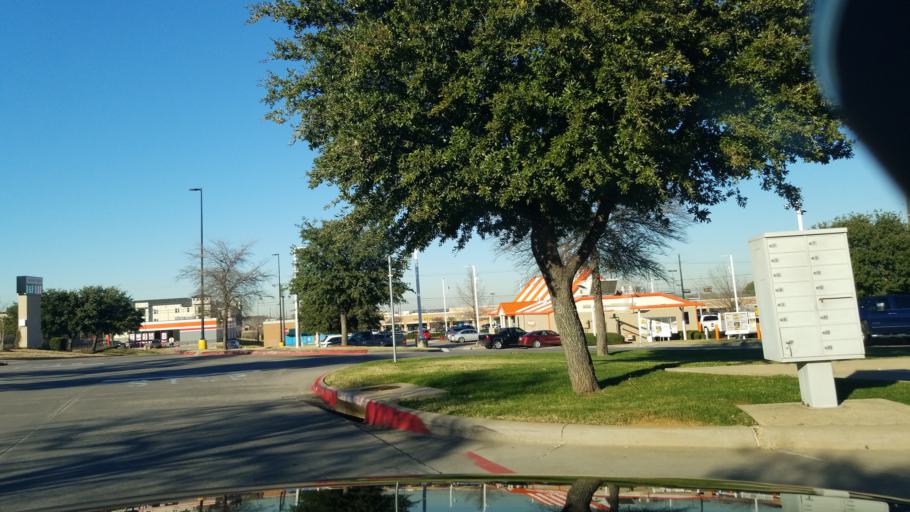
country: US
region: Texas
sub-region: Denton County
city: Hickory Creek
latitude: 33.1289
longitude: -97.0444
